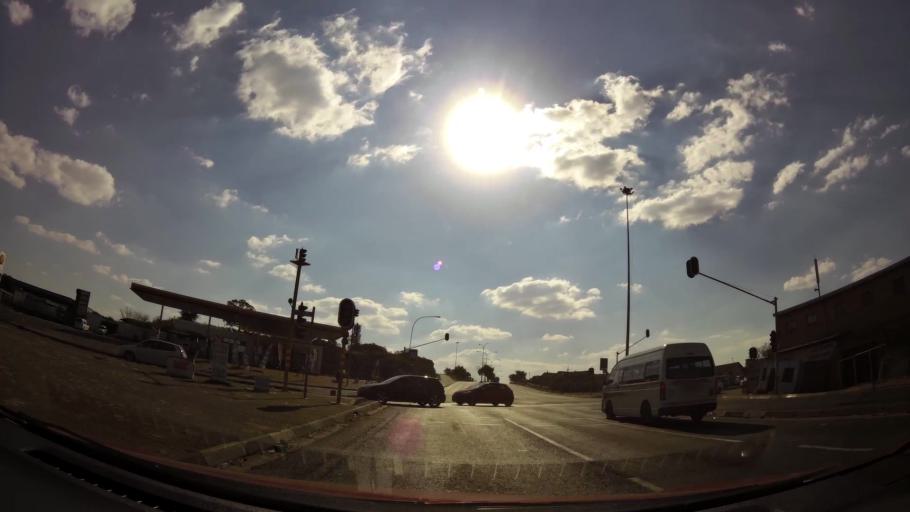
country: ZA
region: Gauteng
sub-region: City of Johannesburg Metropolitan Municipality
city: Soweto
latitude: -26.2319
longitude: 27.8745
